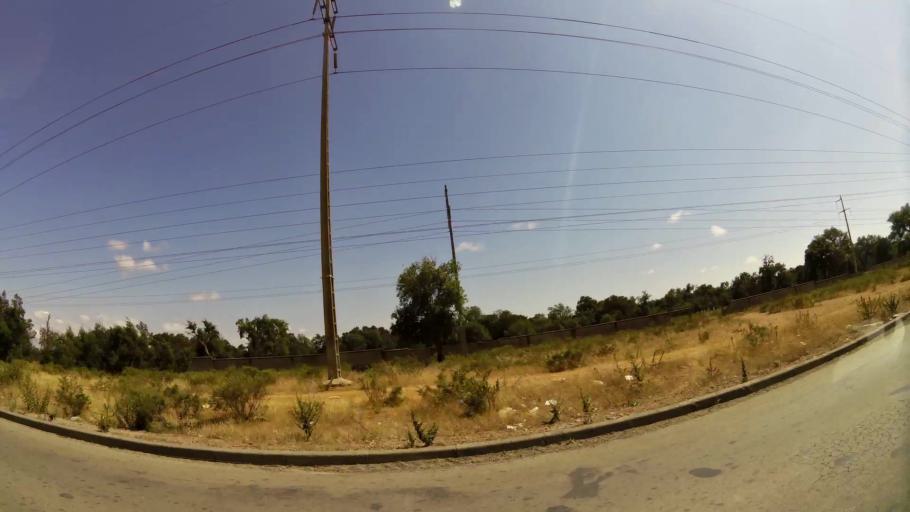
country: MA
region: Gharb-Chrarda-Beni Hssen
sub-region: Kenitra Province
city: Kenitra
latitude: 34.2369
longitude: -6.5612
